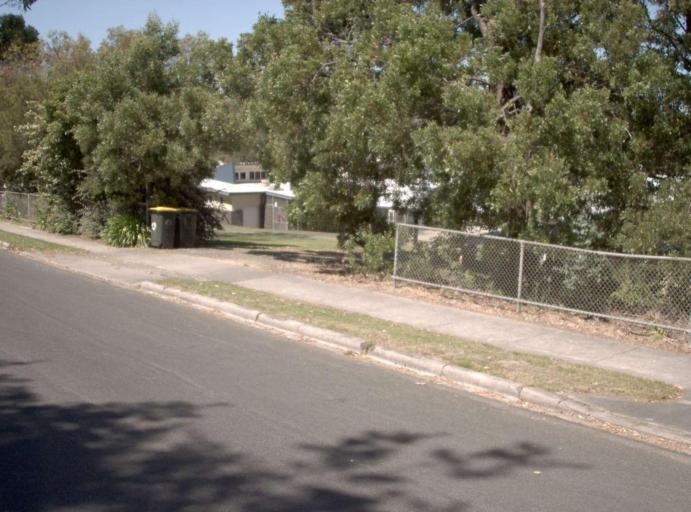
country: AU
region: Victoria
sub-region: Latrobe
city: Morwell
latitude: -38.6528
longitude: 146.1956
